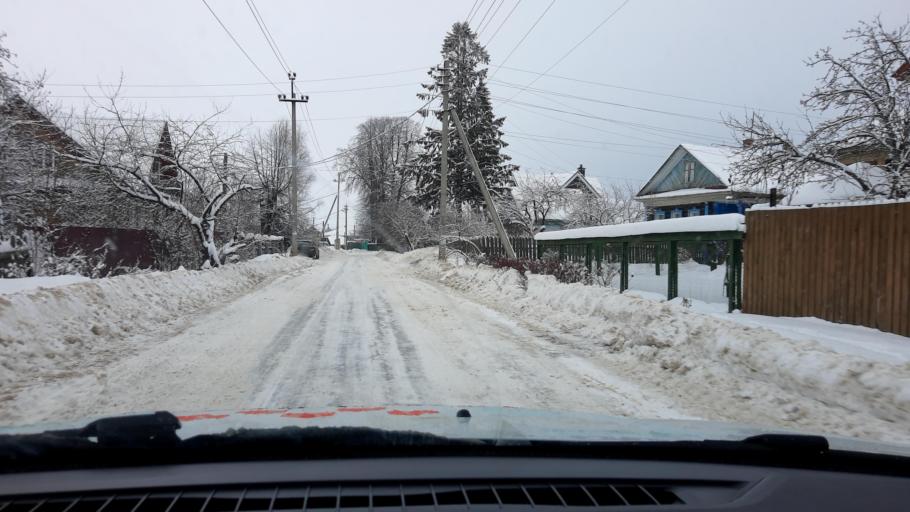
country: RU
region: Nizjnij Novgorod
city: Chkalovsk
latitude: 56.7670
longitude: 43.2636
